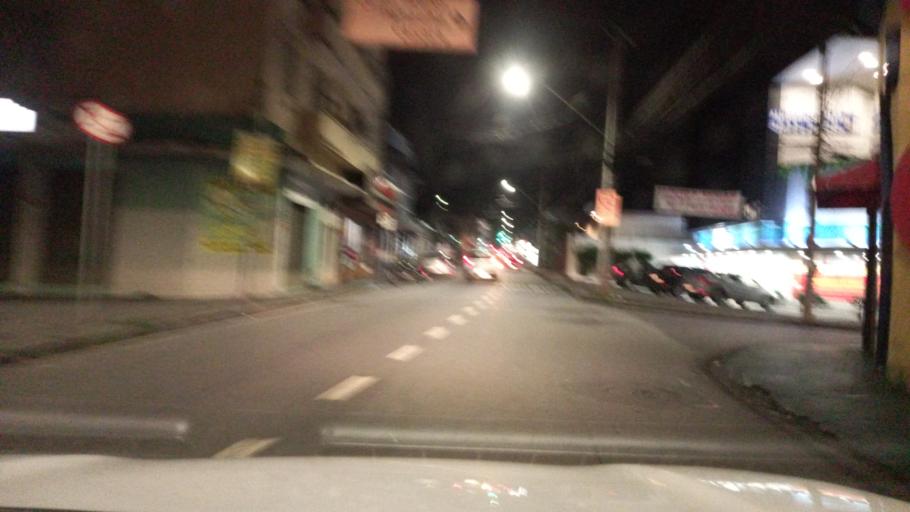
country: BR
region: Minas Gerais
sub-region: Belo Horizonte
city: Belo Horizonte
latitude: -19.9153
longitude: -43.9715
